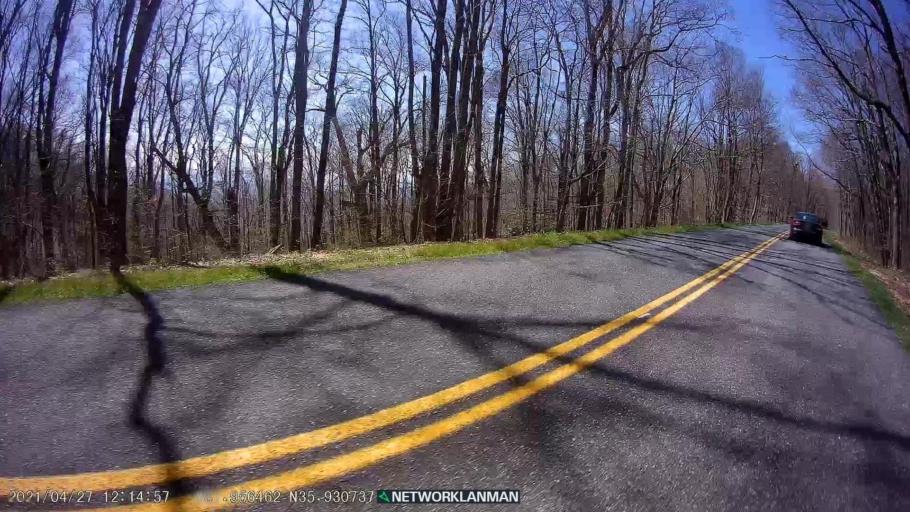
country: US
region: North Carolina
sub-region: Mitchell County
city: Spruce Pine
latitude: 35.9309
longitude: -81.9566
